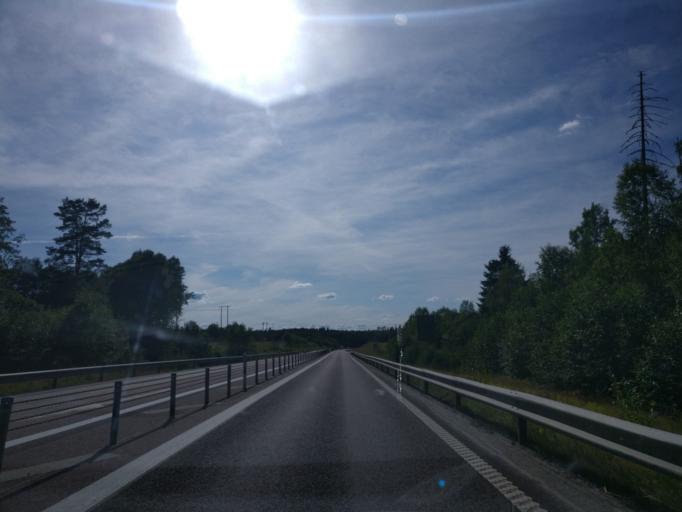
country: SE
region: Vaermland
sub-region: Kils Kommun
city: Kil
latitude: 59.5099
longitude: 13.2334
